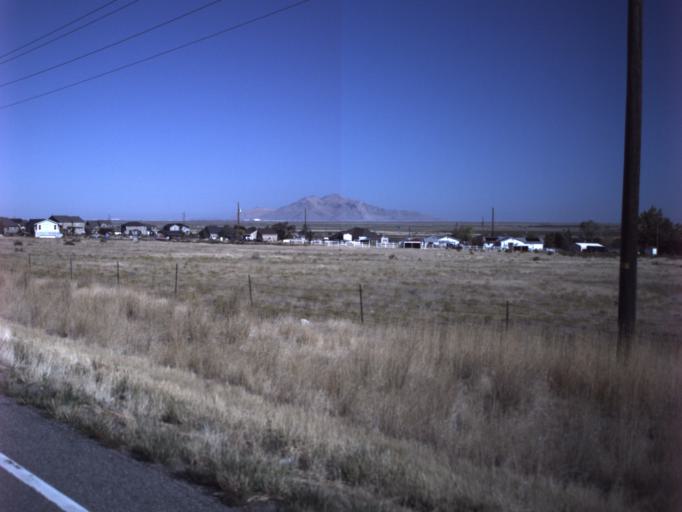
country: US
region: Utah
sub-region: Tooele County
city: Grantsville
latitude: 40.6145
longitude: -112.4970
